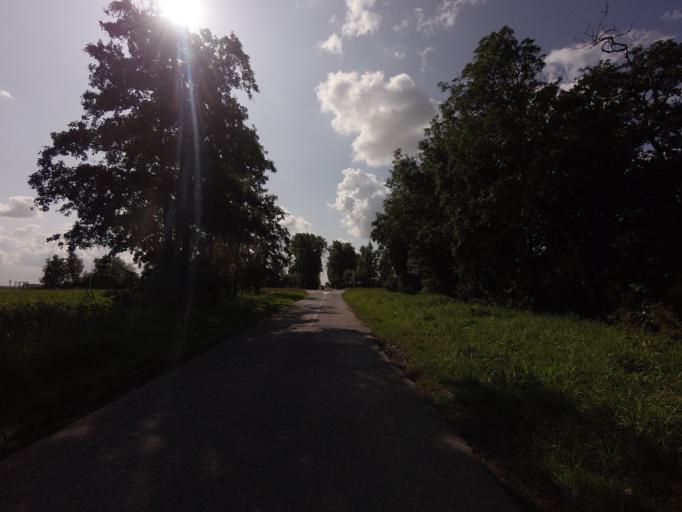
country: NL
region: Friesland
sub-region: Gemeente Het Bildt
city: Sint Annaparochie
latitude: 53.2786
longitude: 5.6758
